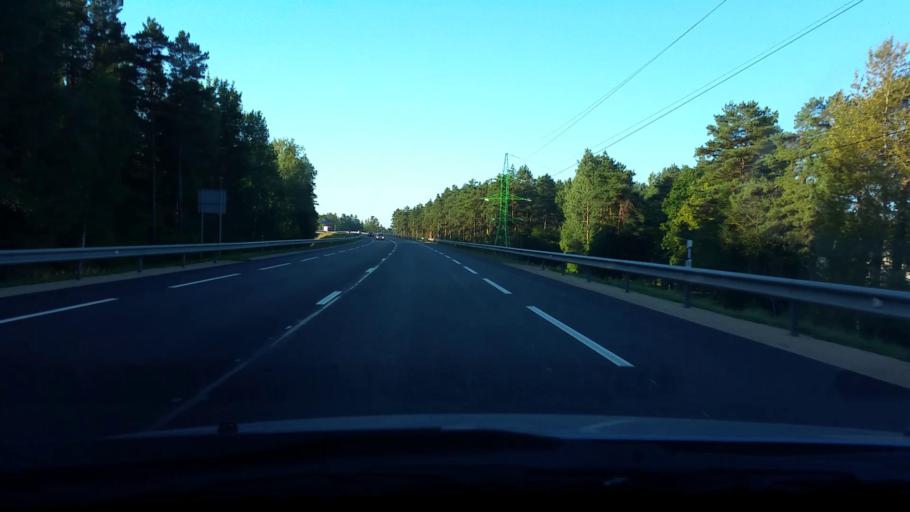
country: LV
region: Riga
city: Bergi
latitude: 57.0142
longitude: 24.3085
